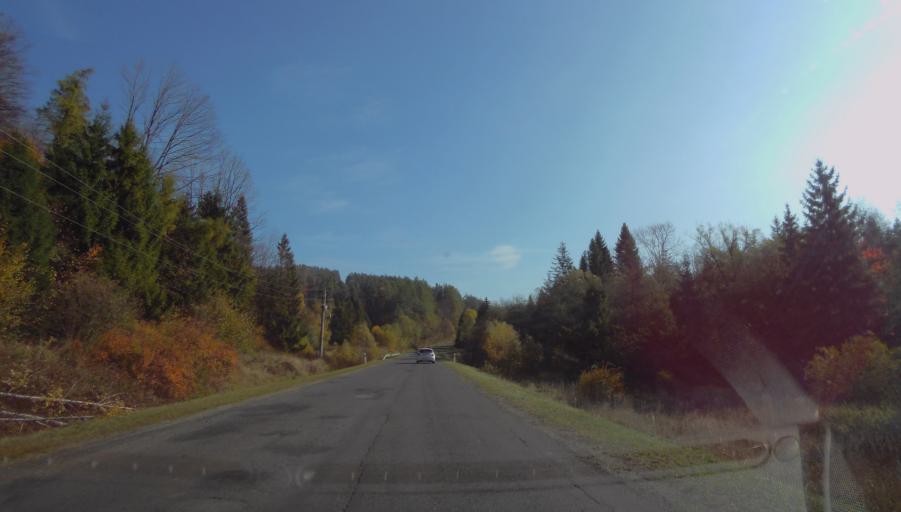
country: PL
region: Subcarpathian Voivodeship
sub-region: Powiat leski
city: Cisna
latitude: 49.2183
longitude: 22.2209
